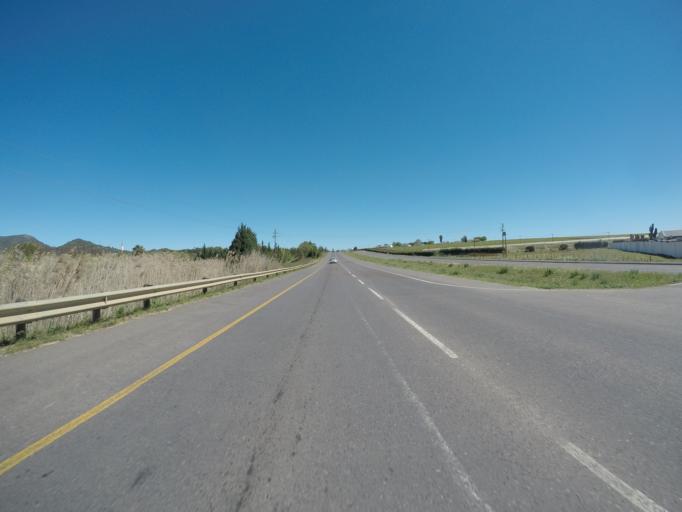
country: ZA
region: Western Cape
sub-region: Cape Winelands District Municipality
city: Noorder-Paarl
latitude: -33.6680
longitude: 18.9172
